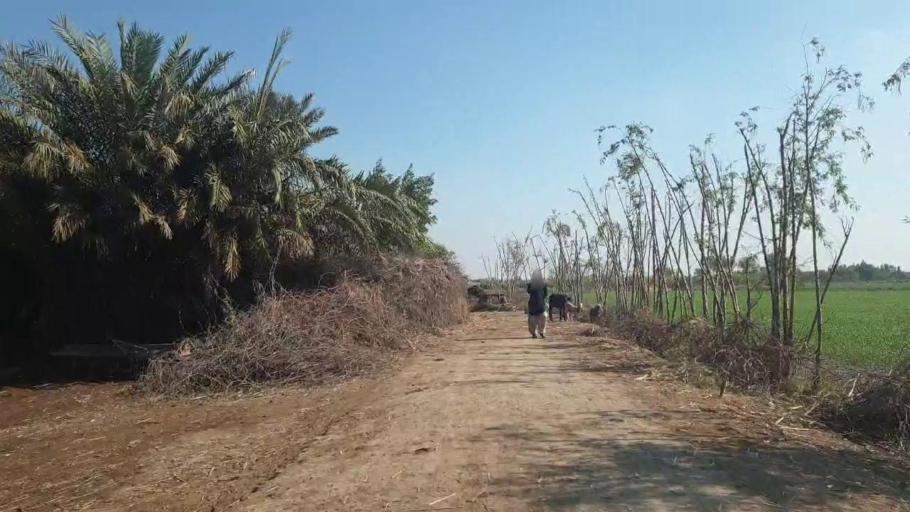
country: PK
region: Sindh
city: Shahdadpur
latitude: 25.9104
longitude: 68.5662
